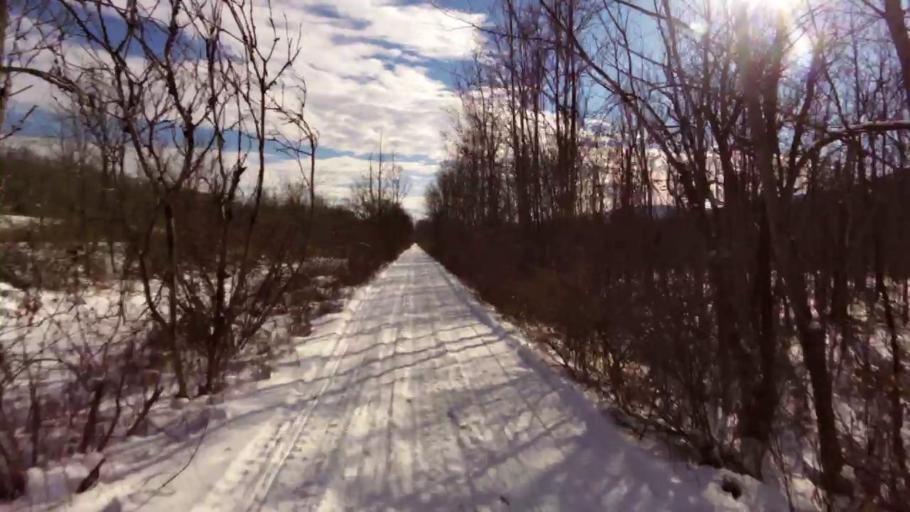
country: US
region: Pennsylvania
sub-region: McKean County
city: Foster Brook
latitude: 42.0537
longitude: -78.6367
